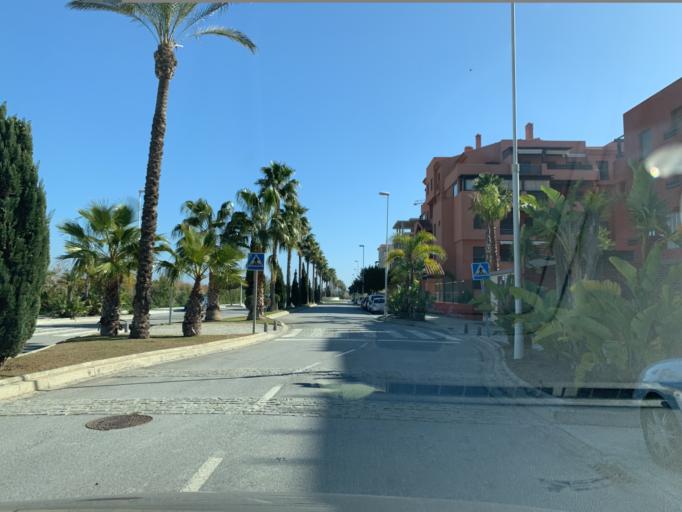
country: ES
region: Andalusia
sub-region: Provincia de Granada
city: El Varadero
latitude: 36.7219
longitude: -3.5541
